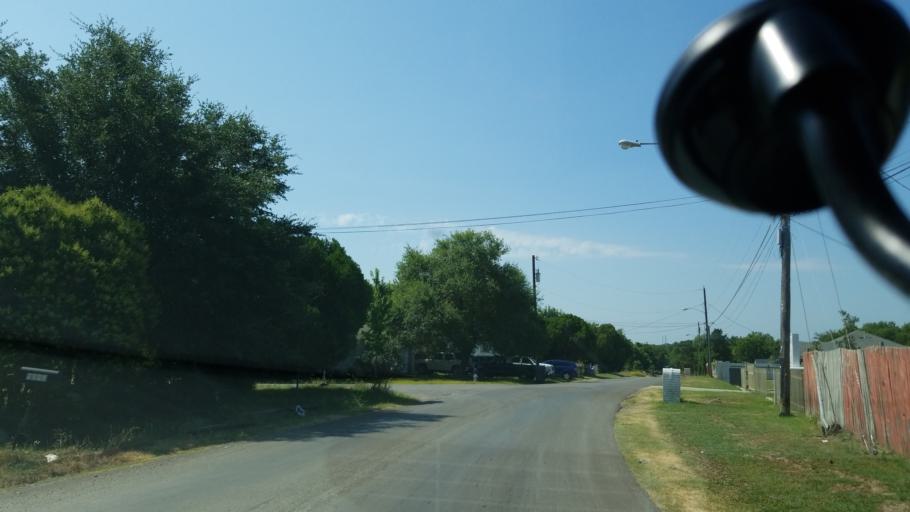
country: US
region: Texas
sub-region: Dallas County
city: Cockrell Hill
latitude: 32.7143
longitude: -96.8775
